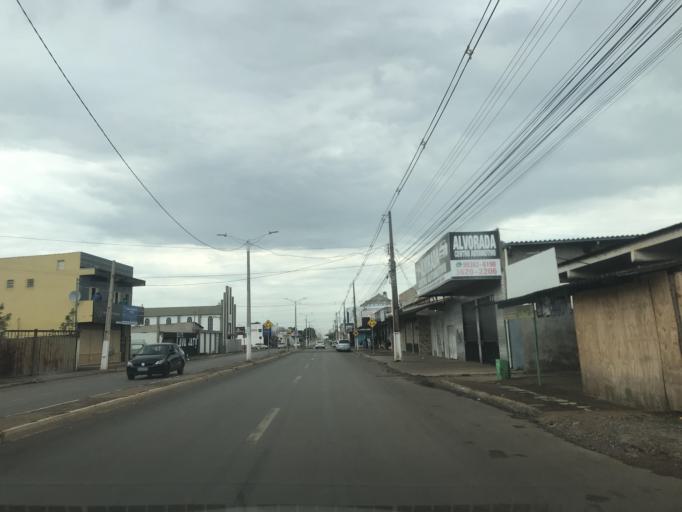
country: BR
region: Goias
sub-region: Luziania
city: Luziania
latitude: -16.2038
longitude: -47.9242
